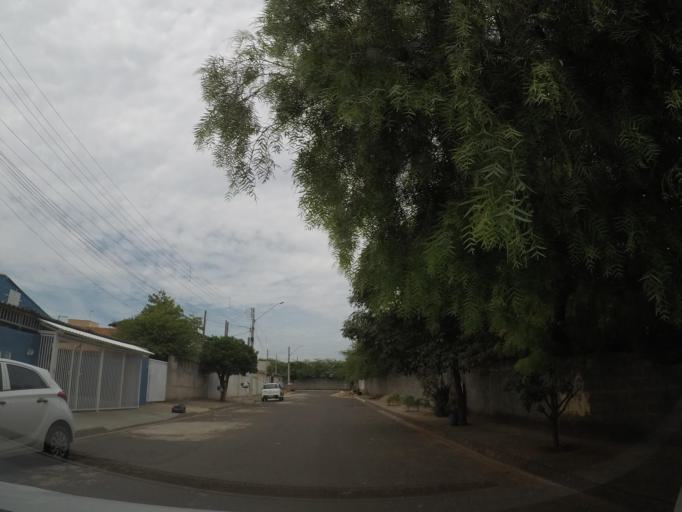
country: BR
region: Sao Paulo
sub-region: Hortolandia
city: Hortolandia
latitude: -22.8339
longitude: -47.1921
